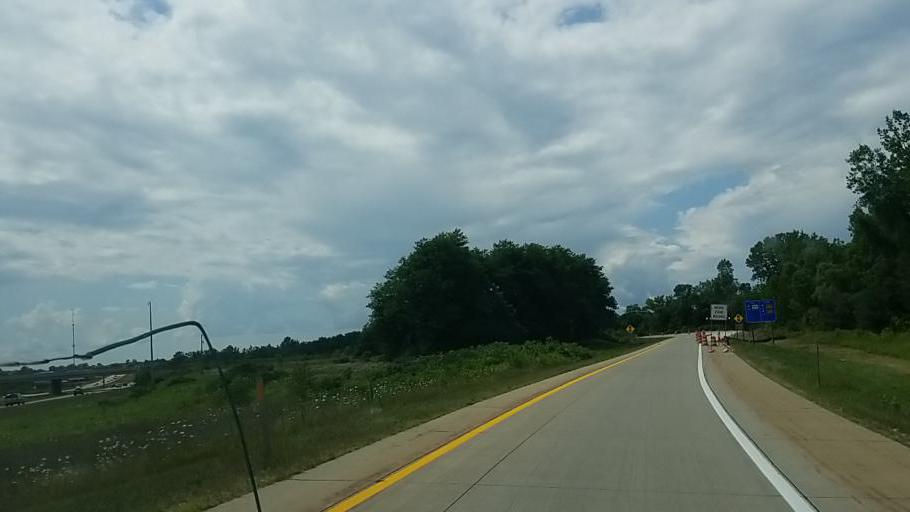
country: US
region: Michigan
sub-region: Kent County
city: Walker
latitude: 43.0222
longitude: -85.7224
